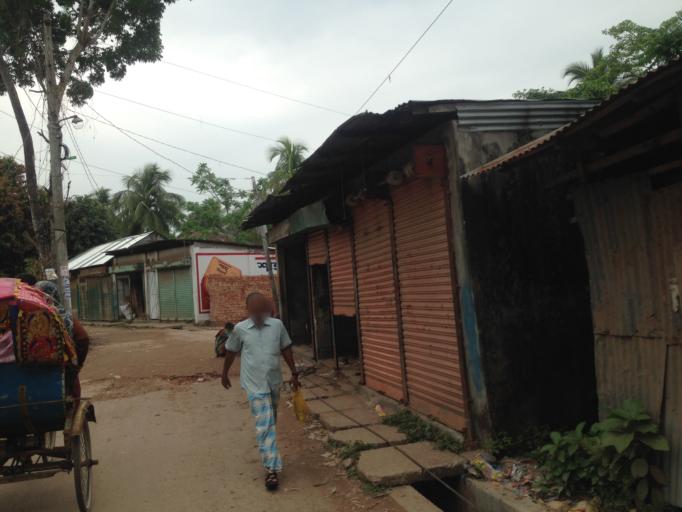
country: BD
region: Chittagong
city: Raipur
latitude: 23.0362
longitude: 90.7702
